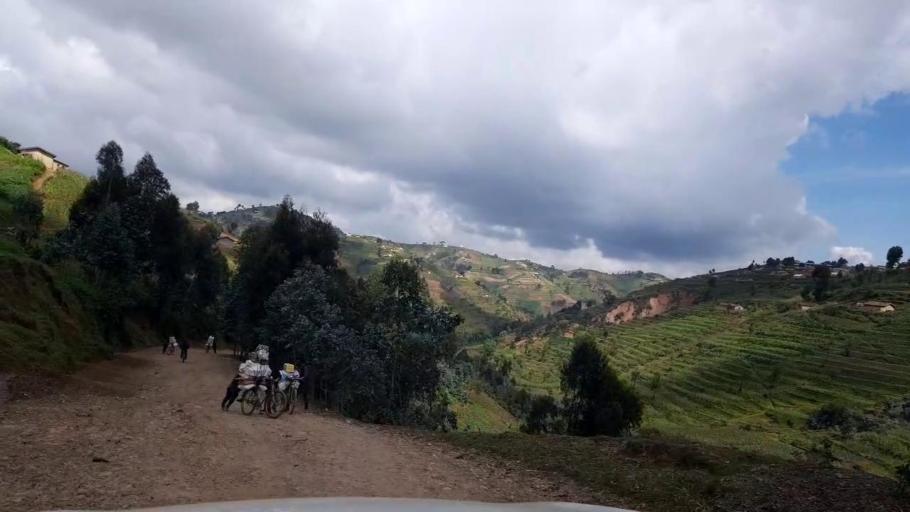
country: RW
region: Western Province
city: Kibuye
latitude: -1.8928
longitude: 29.4593
